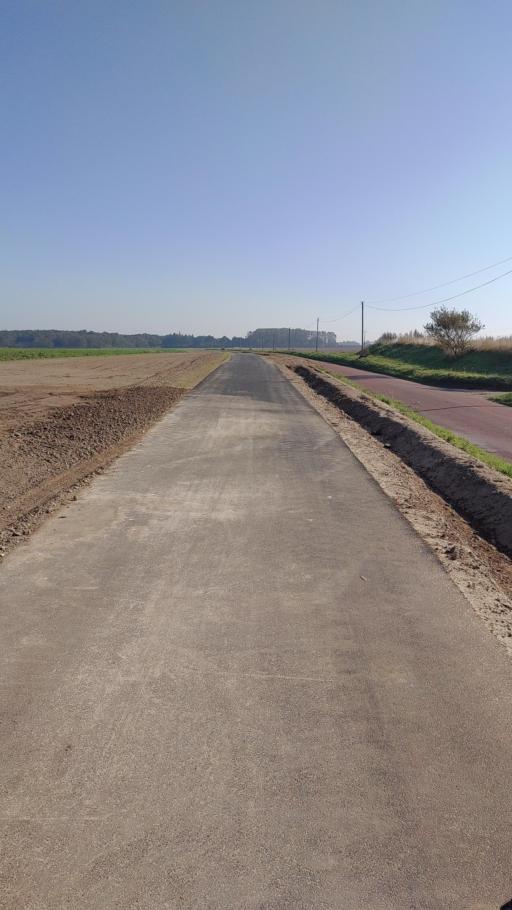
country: FR
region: Picardie
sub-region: Departement de la Somme
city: Mers-les-Bains
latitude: 50.0741
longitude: 1.4011
